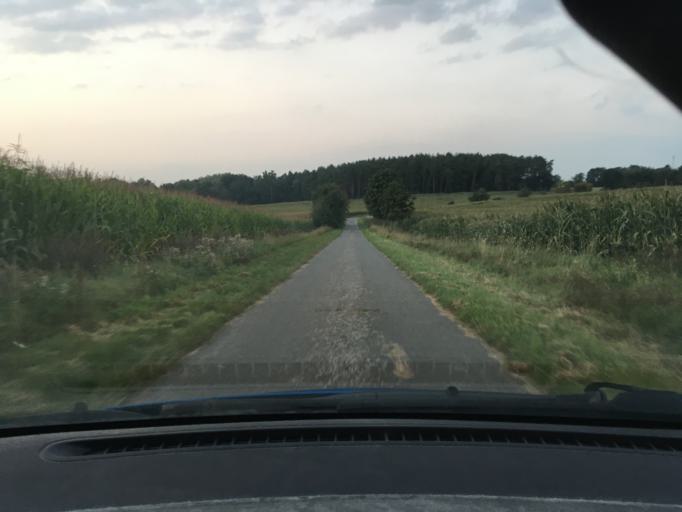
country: DE
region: Lower Saxony
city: Altenmedingen
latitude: 53.1835
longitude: 10.6228
